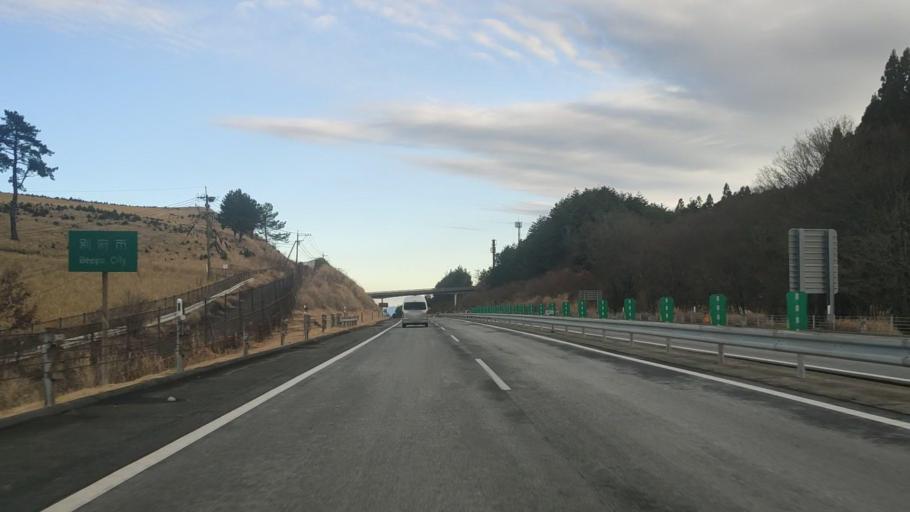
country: JP
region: Oita
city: Beppu
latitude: 33.3188
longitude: 131.4116
